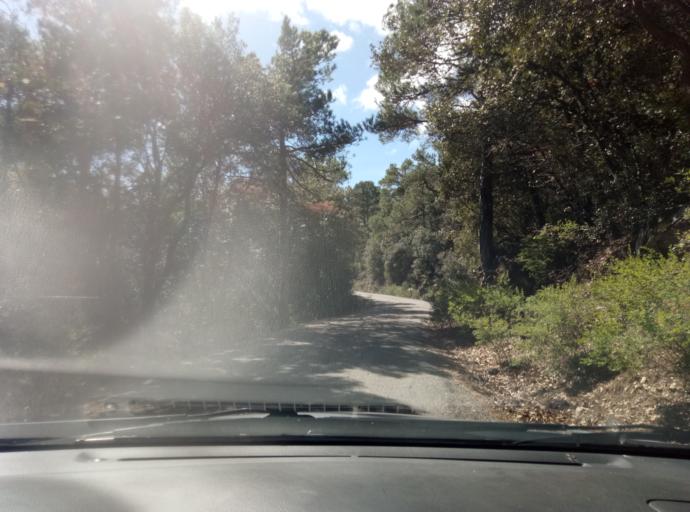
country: ES
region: Catalonia
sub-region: Provincia de Tarragona
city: Vimbodi
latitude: 41.3522
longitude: 1.0602
